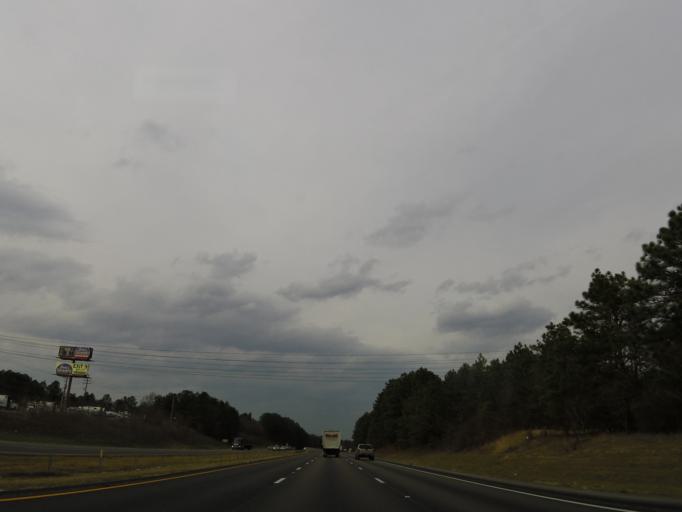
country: US
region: South Carolina
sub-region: Lexington County
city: Pineridge
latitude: 33.8704
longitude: -81.0344
